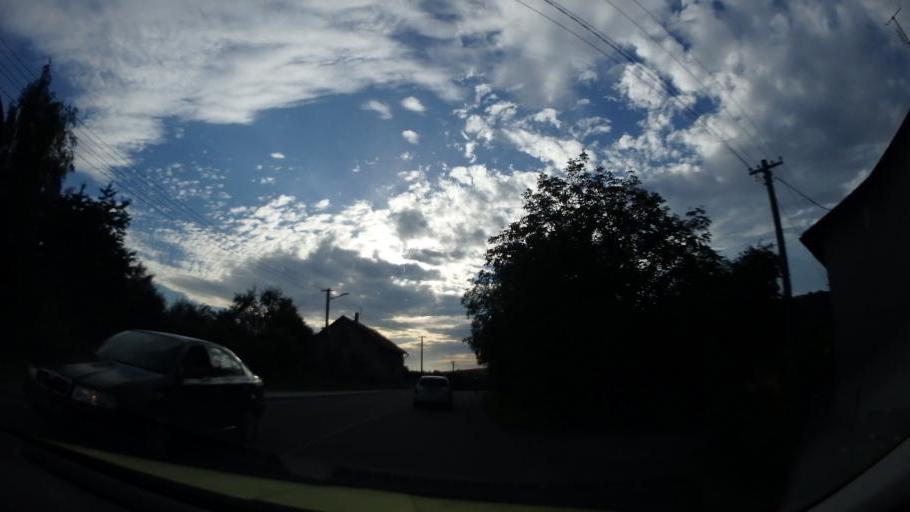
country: CZ
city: Rybi
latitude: 49.5985
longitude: 18.0856
